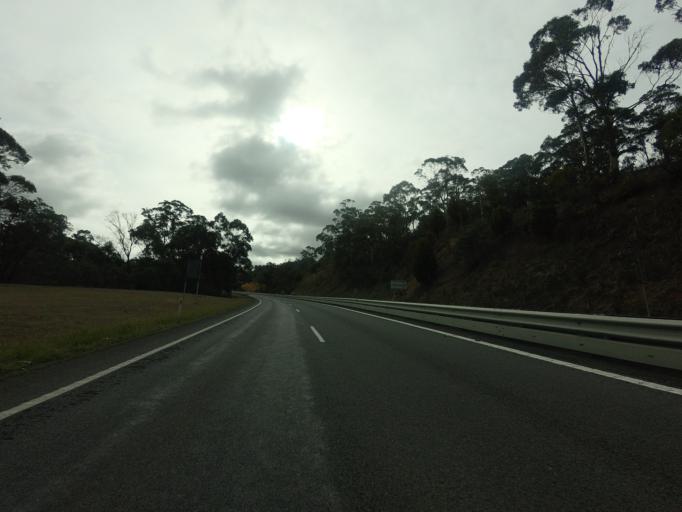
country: AU
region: Tasmania
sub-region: Brighton
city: Bridgewater
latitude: -42.5806
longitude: 147.2289
